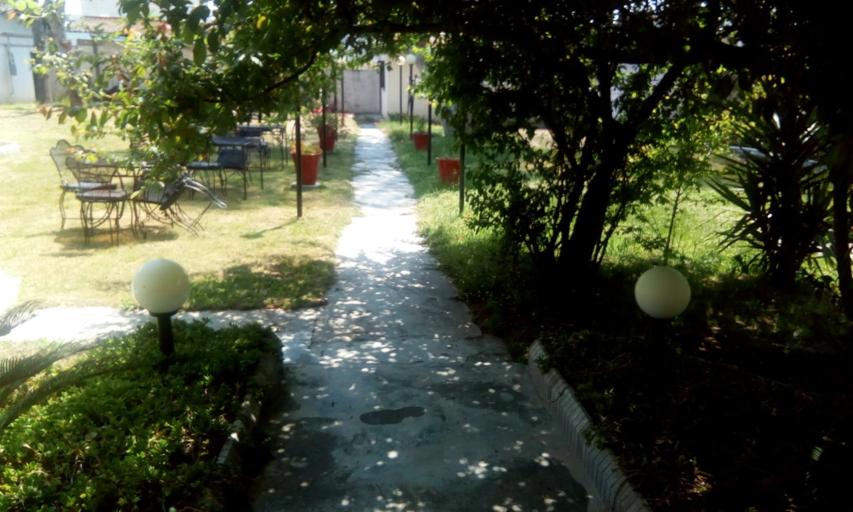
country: IR
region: Mazandaran
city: Babolsar
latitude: 36.7082
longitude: 52.6446
